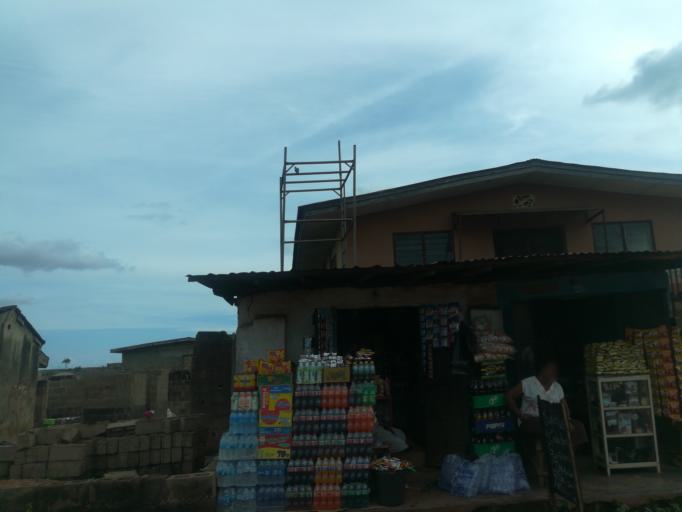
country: NG
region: Oyo
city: Ibadan
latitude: 7.3796
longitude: 3.9487
